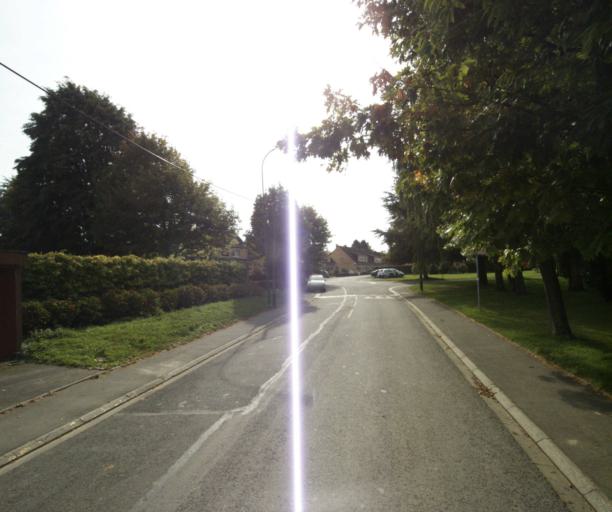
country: FR
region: Nord-Pas-de-Calais
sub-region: Departement du Nord
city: Radinghem-en-Weppes
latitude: 50.6055
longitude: 2.9151
